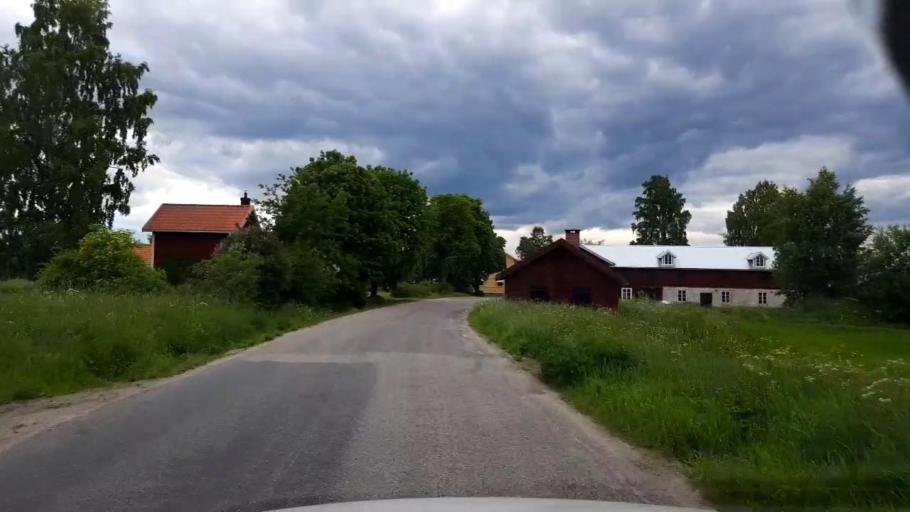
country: SE
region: Gaevleborg
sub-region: Hudiksvalls Kommun
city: Delsbo
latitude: 61.8222
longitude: 16.5496
